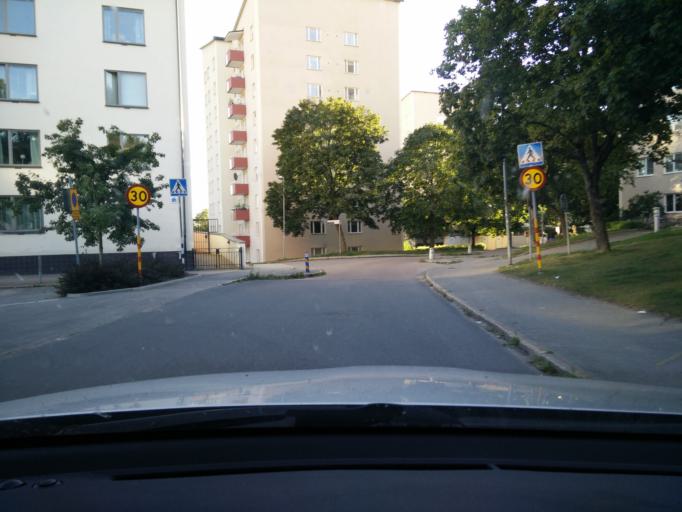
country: SE
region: Stockholm
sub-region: Sollentuna Kommun
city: Sollentuna
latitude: 59.4460
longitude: 17.9648
